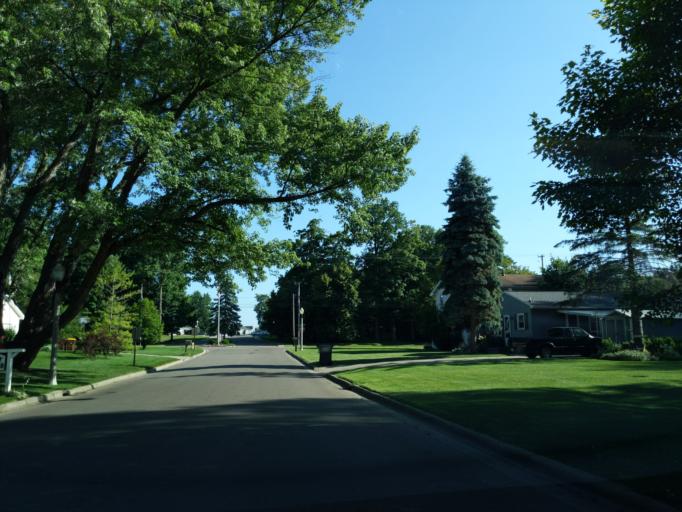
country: US
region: Michigan
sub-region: Eaton County
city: Waverly
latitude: 42.7345
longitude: -84.6183
